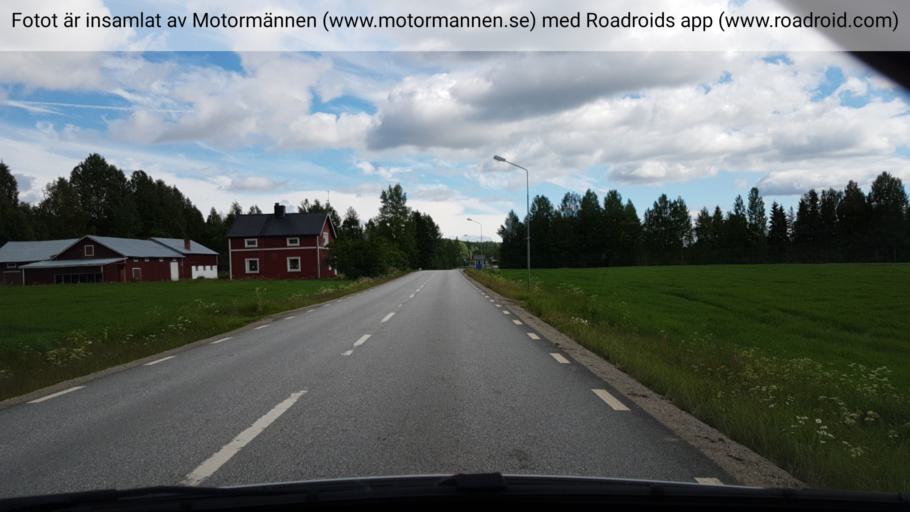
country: SE
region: Vaesterbotten
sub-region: Vindelns Kommun
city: Vindeln
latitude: 64.1672
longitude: 19.4948
